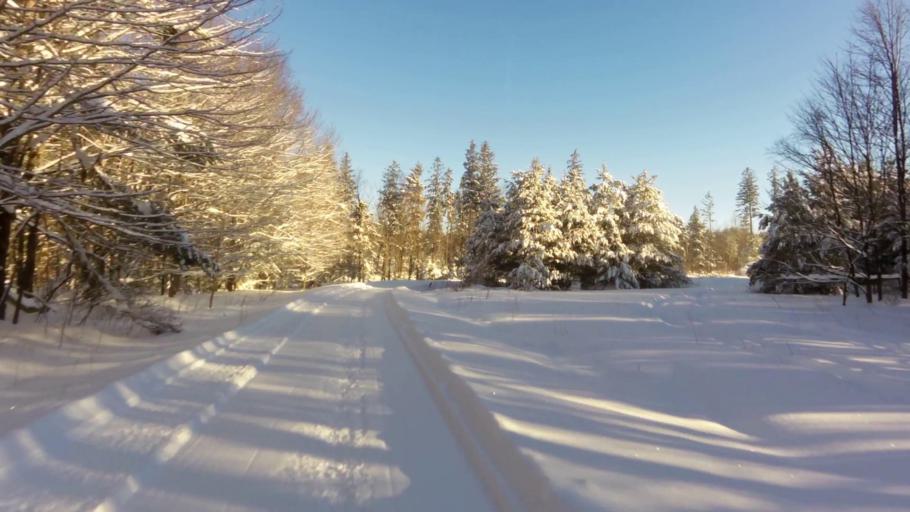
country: US
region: New York
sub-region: Chautauqua County
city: Falconer
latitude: 42.2396
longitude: -79.2178
